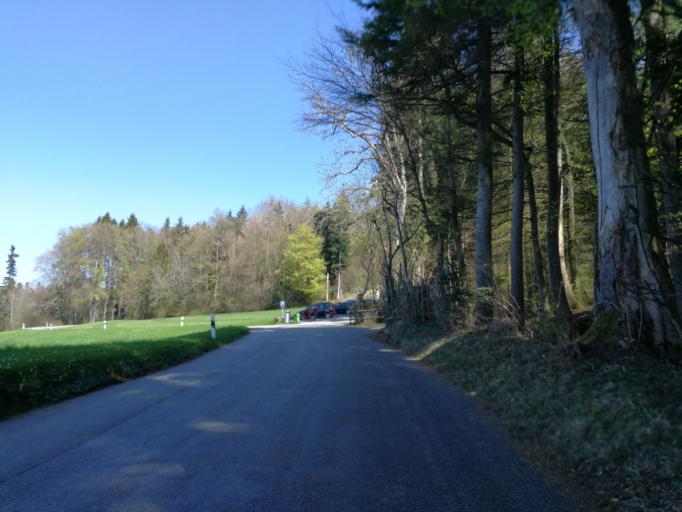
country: CH
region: Zurich
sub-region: Bezirk Uster
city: Aesch
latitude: 47.3050
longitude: 8.6451
